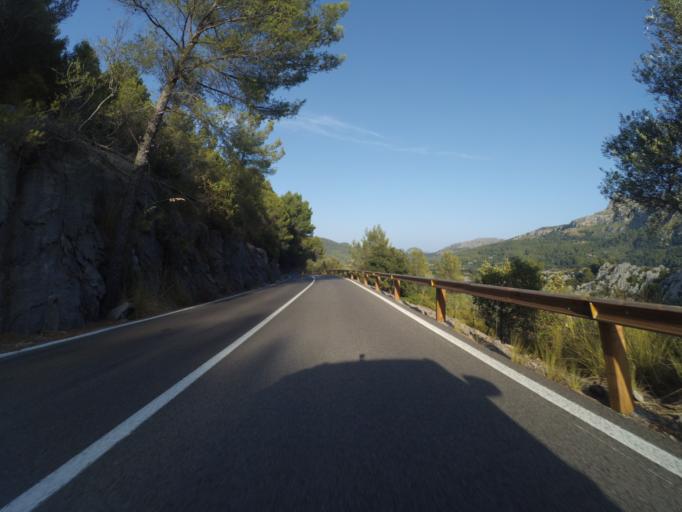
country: ES
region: Balearic Islands
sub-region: Illes Balears
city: Pollenca
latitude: 39.8660
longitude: 2.9407
